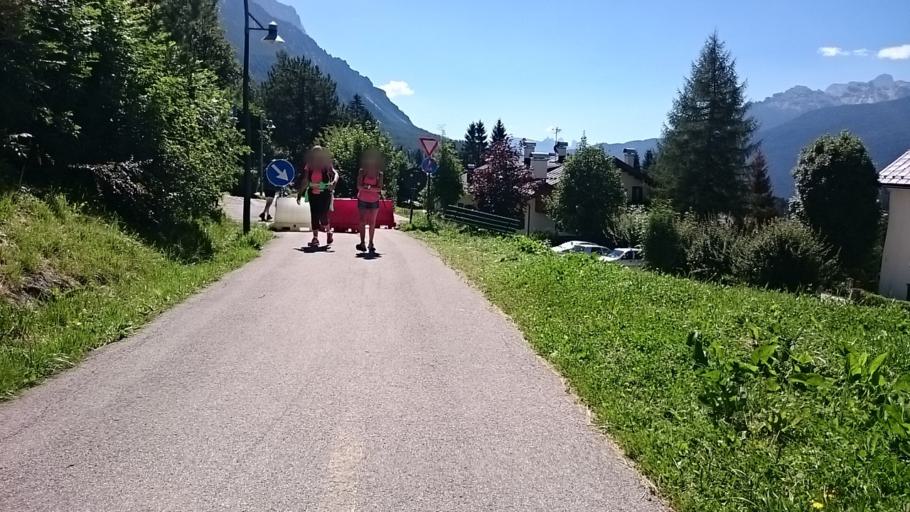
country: IT
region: Veneto
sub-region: Provincia di Belluno
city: Cortina d'Ampezzo
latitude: 46.5500
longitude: 12.1312
